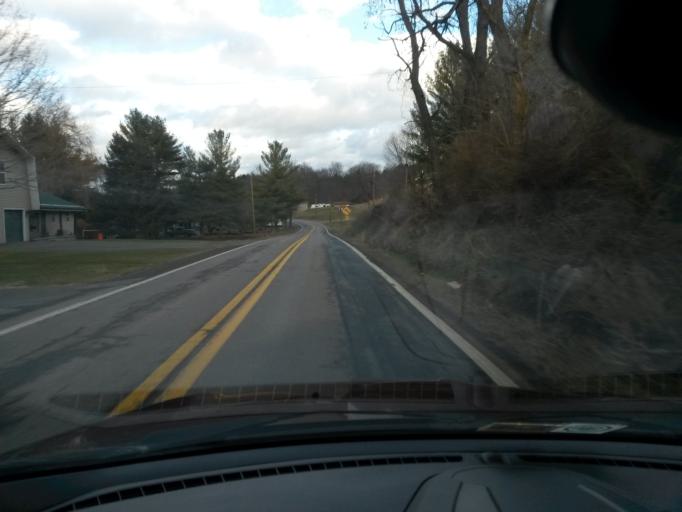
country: US
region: West Virginia
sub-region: Monroe County
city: Union
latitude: 37.5740
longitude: -80.5536
